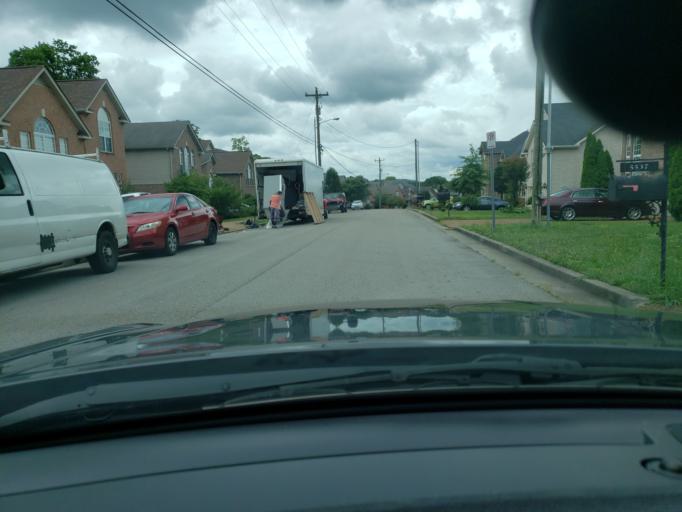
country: US
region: Tennessee
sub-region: Williamson County
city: Nolensville
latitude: 36.0340
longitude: -86.6822
